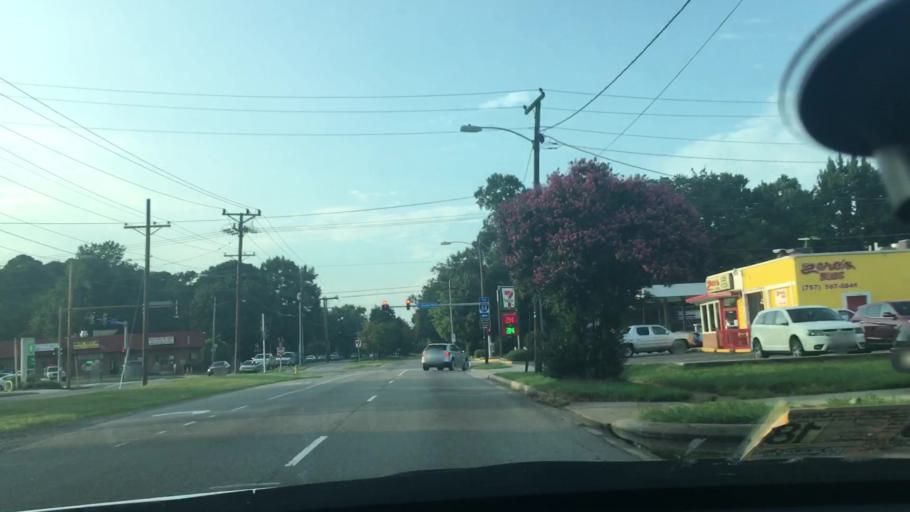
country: US
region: Virginia
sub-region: City of Norfolk
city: Norfolk
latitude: 36.9332
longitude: -76.2442
